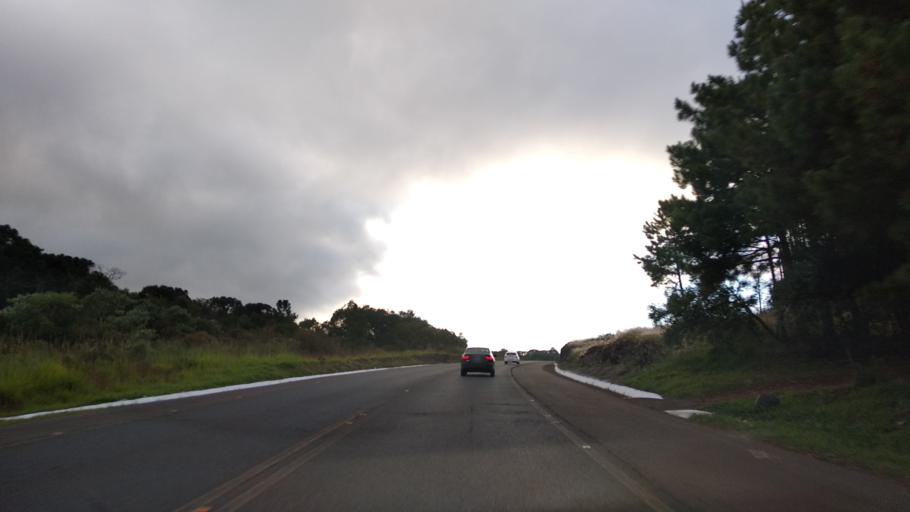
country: BR
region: Santa Catarina
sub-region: Curitibanos
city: Curitibanos
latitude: -27.5788
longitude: -50.7686
